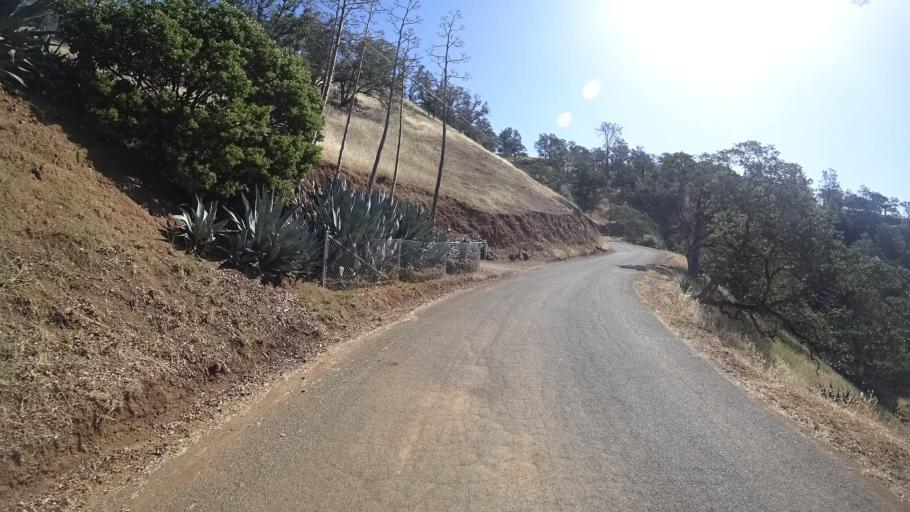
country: US
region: California
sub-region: Lake County
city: Clearlake Oaks
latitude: 39.0056
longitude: -122.7261
